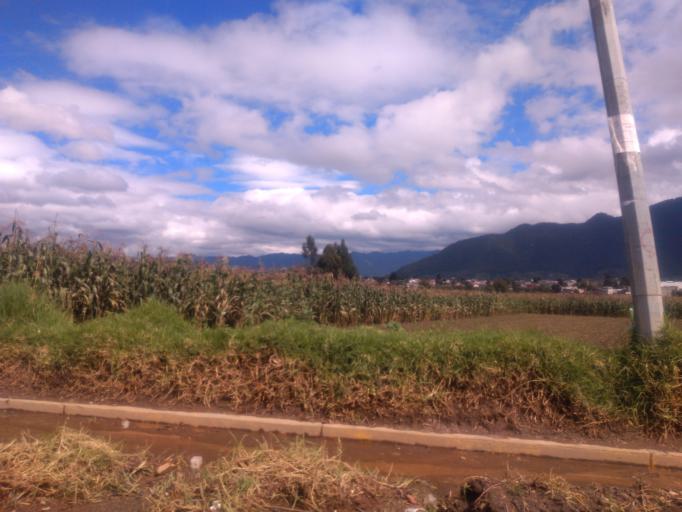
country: GT
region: Quetzaltenango
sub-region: Municipio de La Esperanza
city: La Esperanza
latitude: 14.8614
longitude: -91.5715
